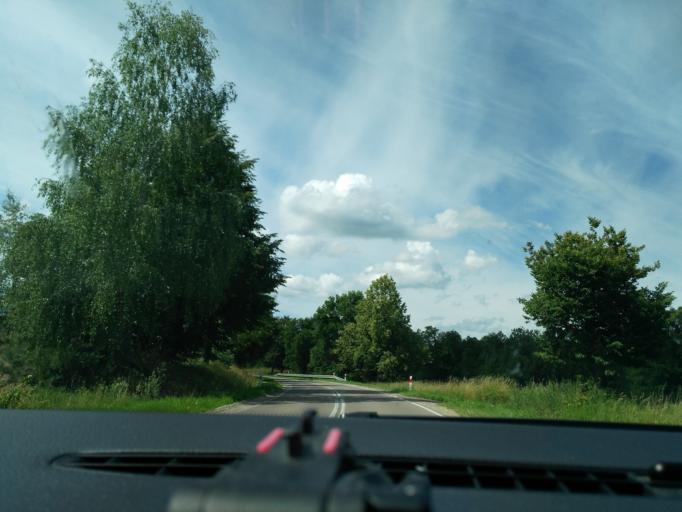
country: PL
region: Podlasie
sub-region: Powiat sejnenski
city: Sejny
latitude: 54.0667
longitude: 23.3579
